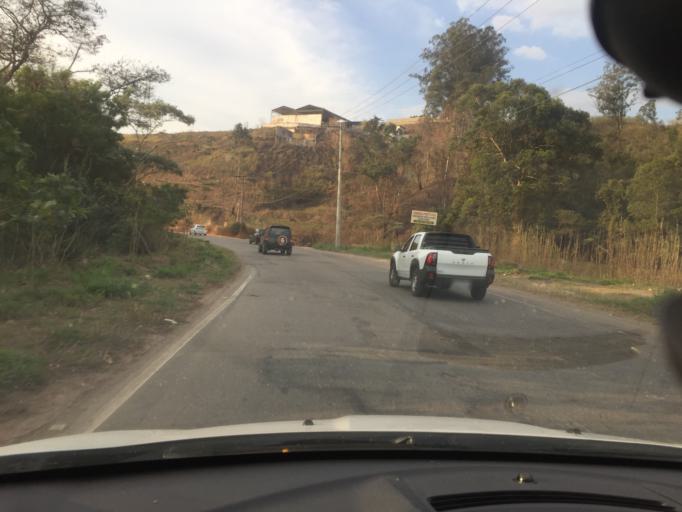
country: BR
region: Sao Paulo
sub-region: Varzea Paulista
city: Varzea Paulista
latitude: -23.2040
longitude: -46.8115
